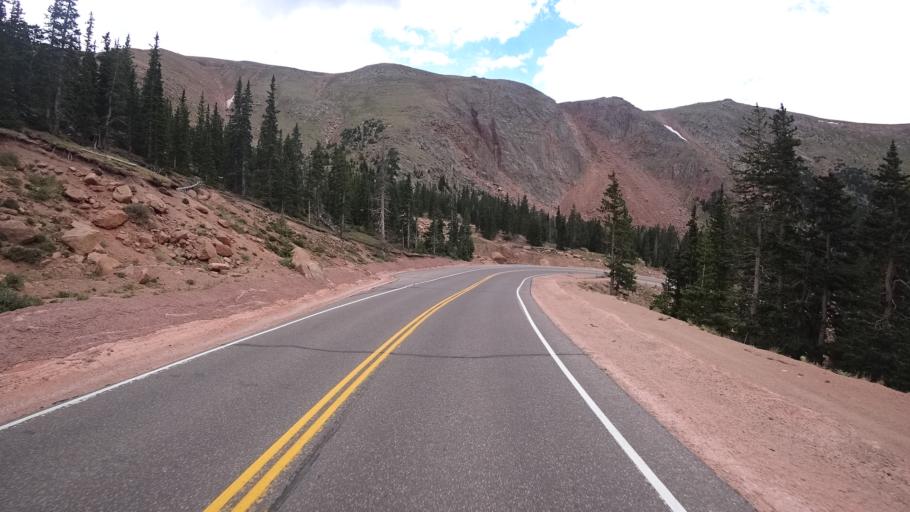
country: US
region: Colorado
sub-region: El Paso County
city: Cascade-Chipita Park
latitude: 38.8729
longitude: -105.0703
